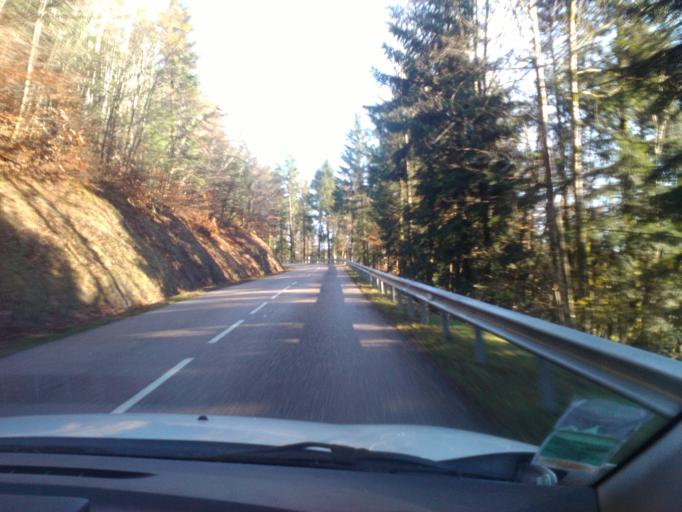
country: FR
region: Lorraine
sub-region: Departement des Vosges
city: Remiremont
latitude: 47.9702
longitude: 6.5335
